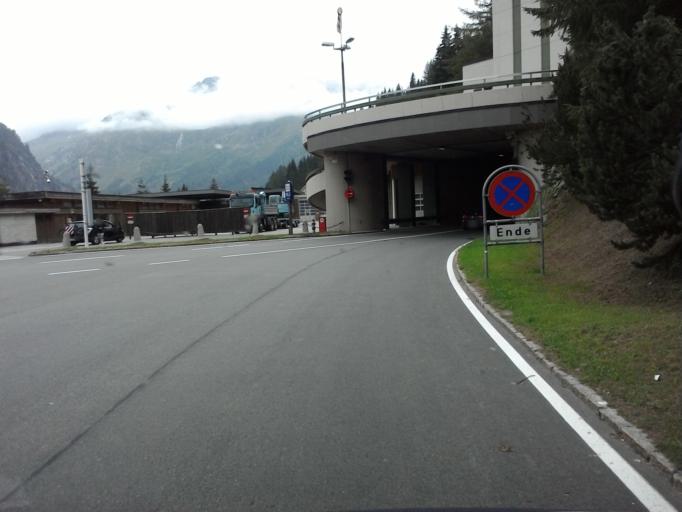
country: AT
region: Tyrol
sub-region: Politischer Bezirk Lienz
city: Matrei in Osttirol
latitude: 47.1178
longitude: 12.5047
